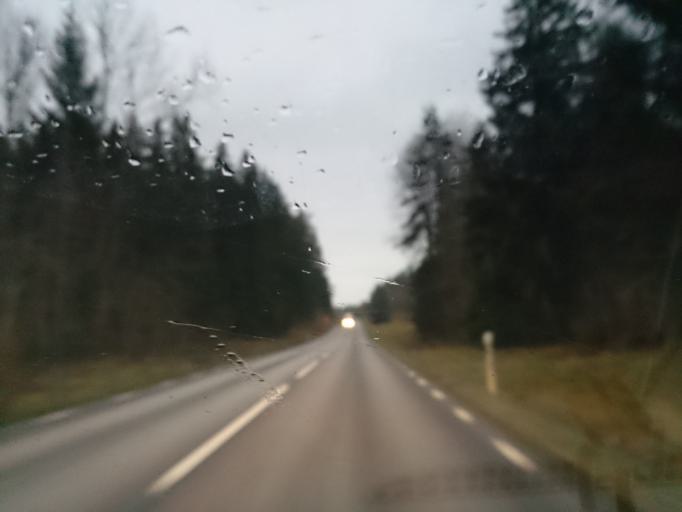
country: SE
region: OEstergoetland
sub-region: Atvidabergs Kommun
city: Atvidaberg
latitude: 58.2476
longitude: 15.9317
